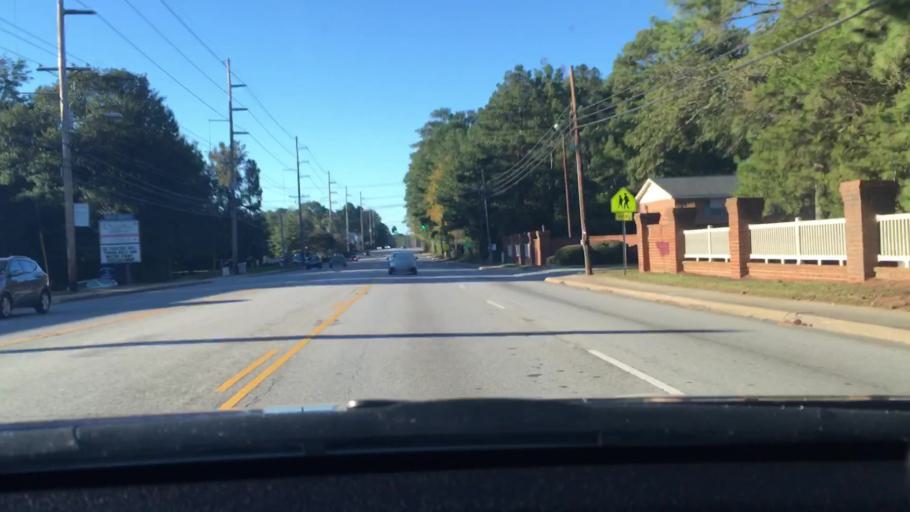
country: US
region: South Carolina
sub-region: Lexington County
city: Saint Andrews
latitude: 34.0596
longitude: -81.1126
